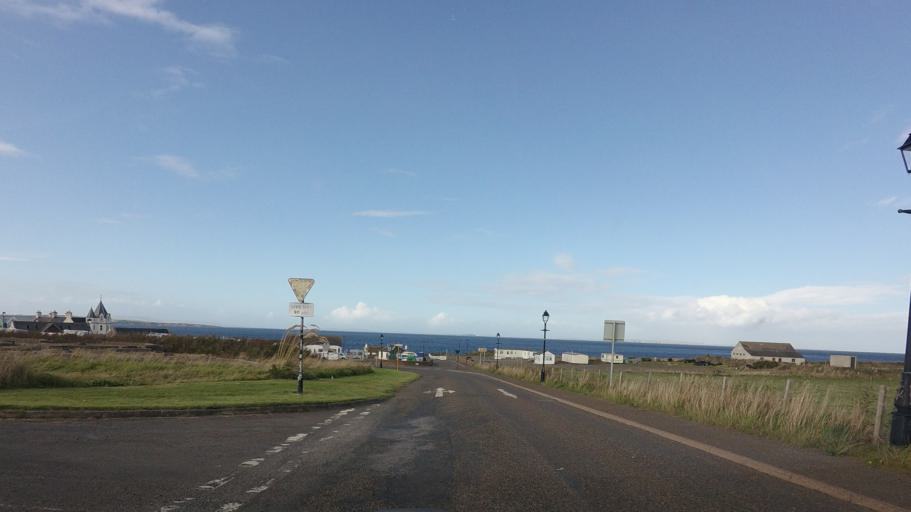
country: GB
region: Scotland
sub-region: Highland
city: Wick
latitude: 58.6423
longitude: -3.0687
